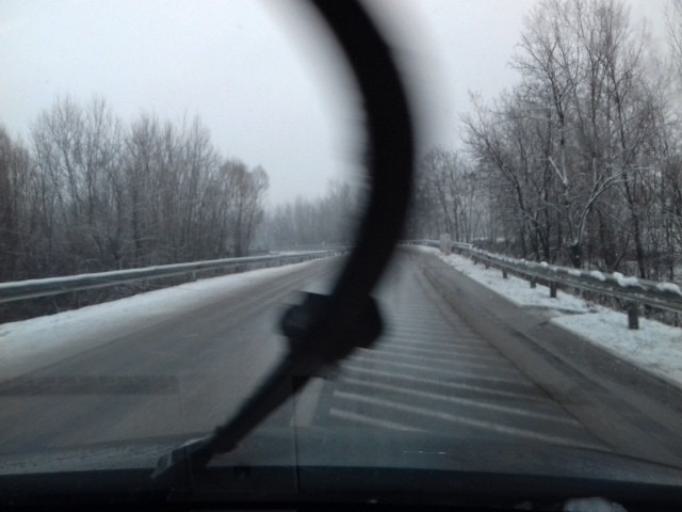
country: HU
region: Budapest
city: Budapest XV. keruelet
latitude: 47.5971
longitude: 19.1319
